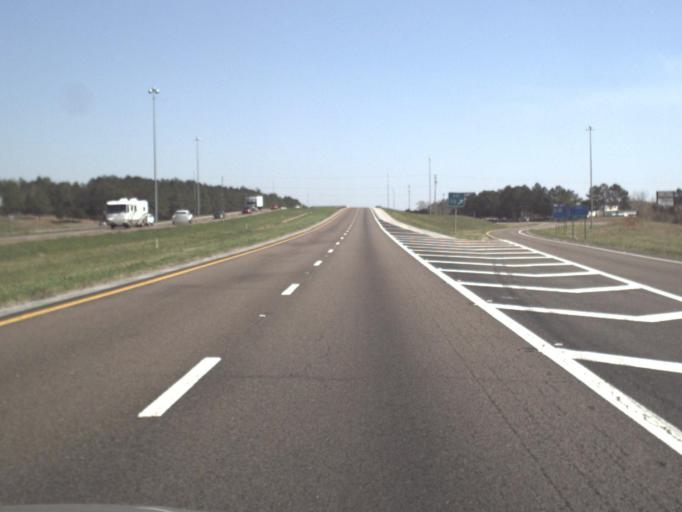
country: US
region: Florida
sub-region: Holmes County
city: Bonifay
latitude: 30.7628
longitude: -85.6895
